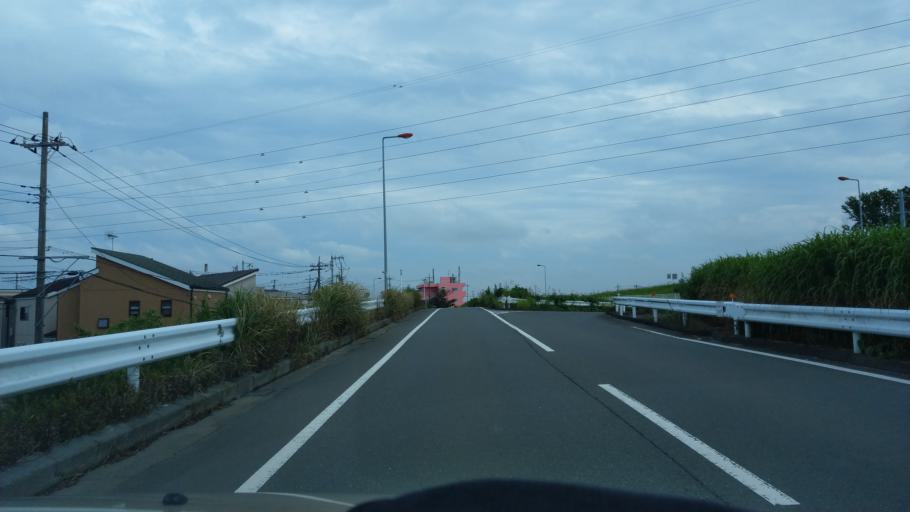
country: JP
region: Saitama
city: Kamifukuoka
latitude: 35.9172
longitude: 139.5570
